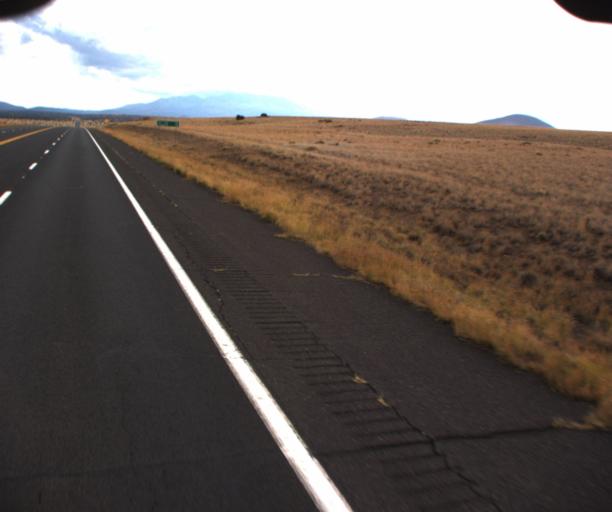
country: US
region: Arizona
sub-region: Coconino County
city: Flagstaff
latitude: 35.5713
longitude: -111.5318
